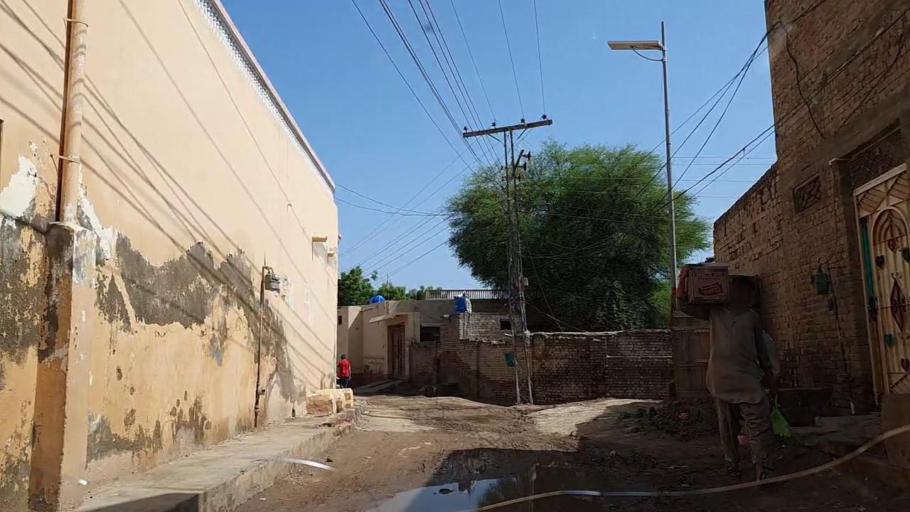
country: PK
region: Sindh
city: Pad Idan
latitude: 26.7727
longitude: 68.3000
